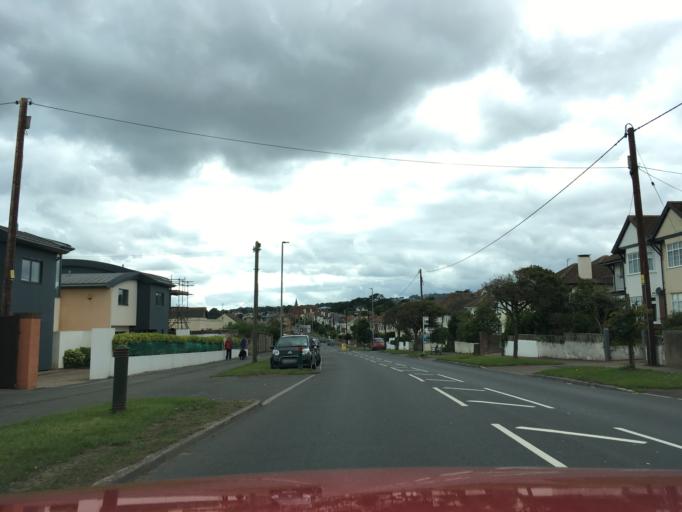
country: GB
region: England
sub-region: Devon
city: Dawlish
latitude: 50.5865
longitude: -3.4572
